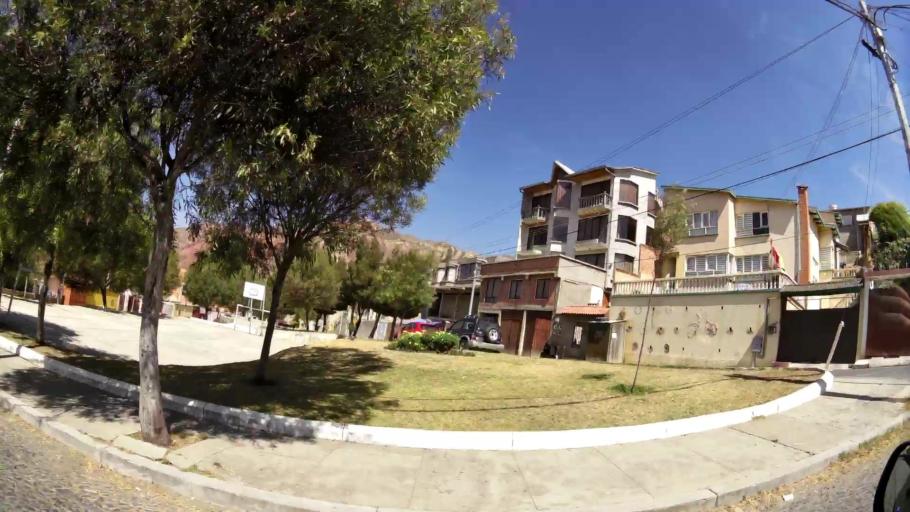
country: BO
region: La Paz
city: La Paz
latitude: -16.5371
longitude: -68.1014
